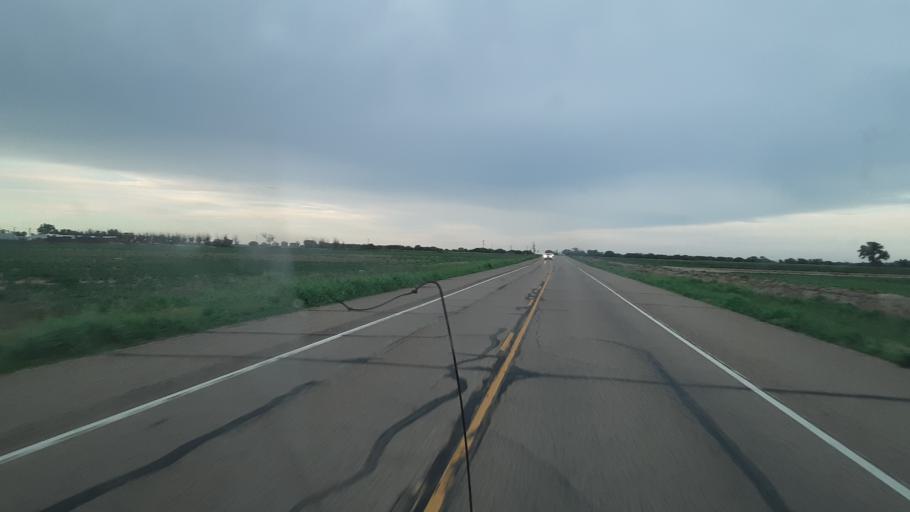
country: US
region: Colorado
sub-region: Prowers County
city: Lamar
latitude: 38.0636
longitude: -102.3534
